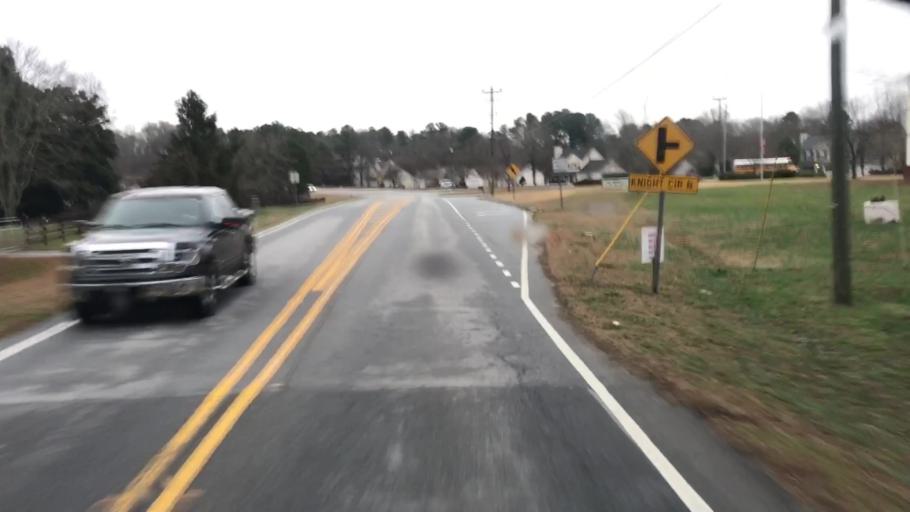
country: US
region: Georgia
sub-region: Walton County
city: Loganville
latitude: 33.8213
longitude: -83.9613
